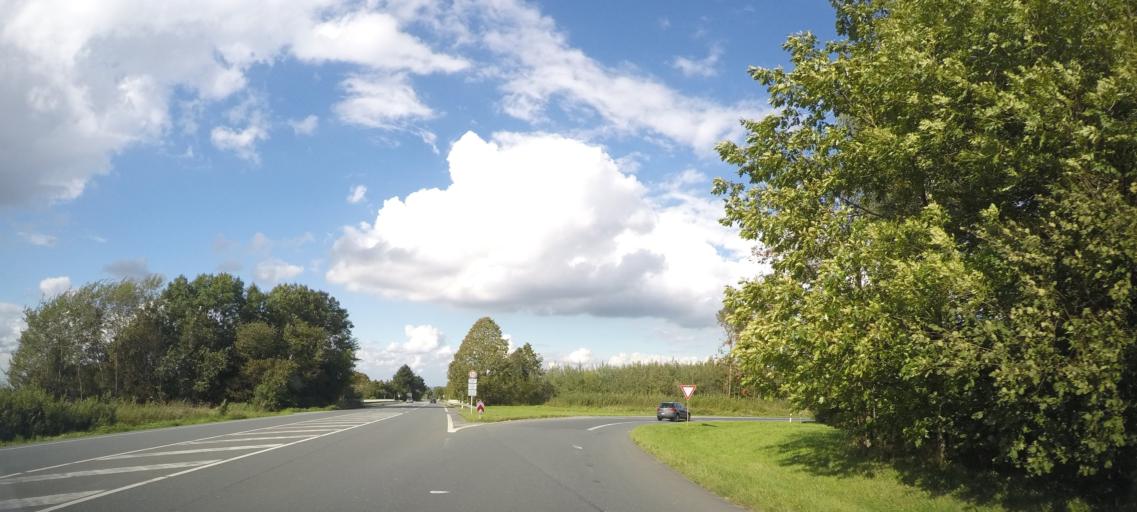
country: DE
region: North Rhine-Westphalia
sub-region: Regierungsbezirk Arnsberg
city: Unna
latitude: 51.5062
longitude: 7.7022
